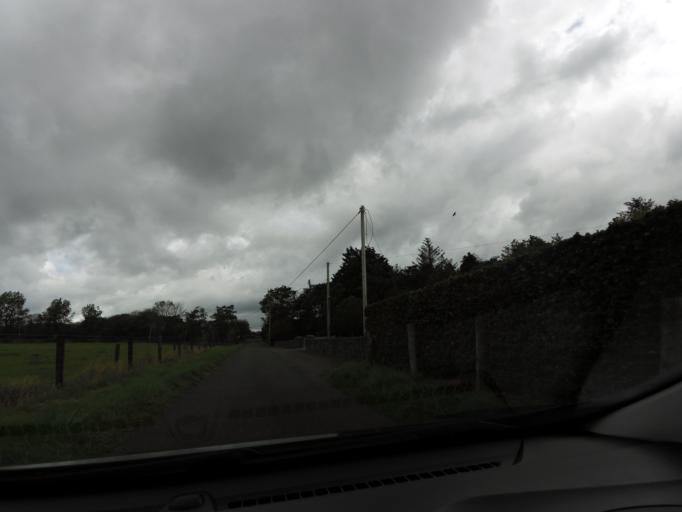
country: IE
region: Connaught
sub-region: County Galway
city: Athenry
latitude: 53.2942
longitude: -8.6984
